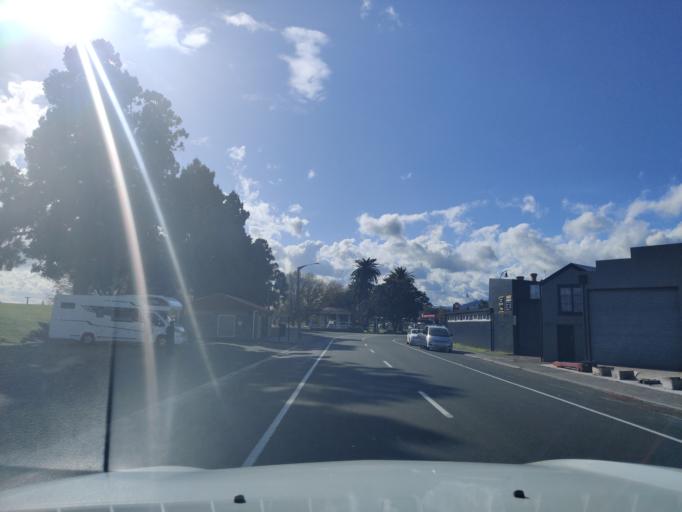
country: NZ
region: Waikato
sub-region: Hauraki District
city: Paeroa
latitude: -37.3778
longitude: 175.6675
